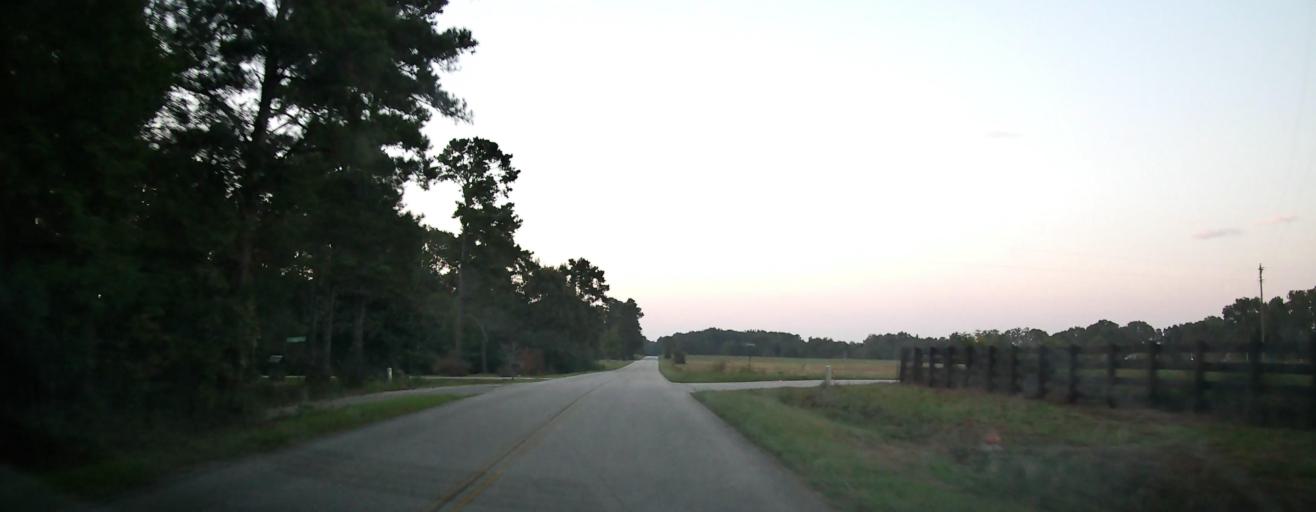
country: US
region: Georgia
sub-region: Butts County
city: Jackson
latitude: 33.3011
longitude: -84.0430
